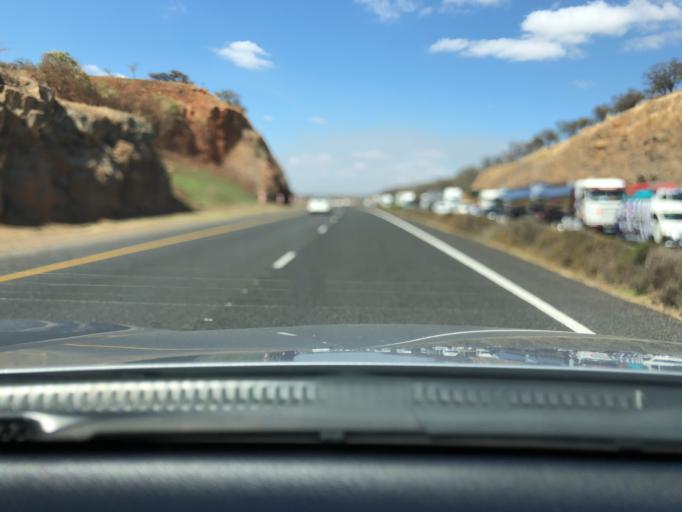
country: ZA
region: KwaZulu-Natal
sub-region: uThukela District Municipality
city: Ladysmith
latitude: -28.7290
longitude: 29.6456
